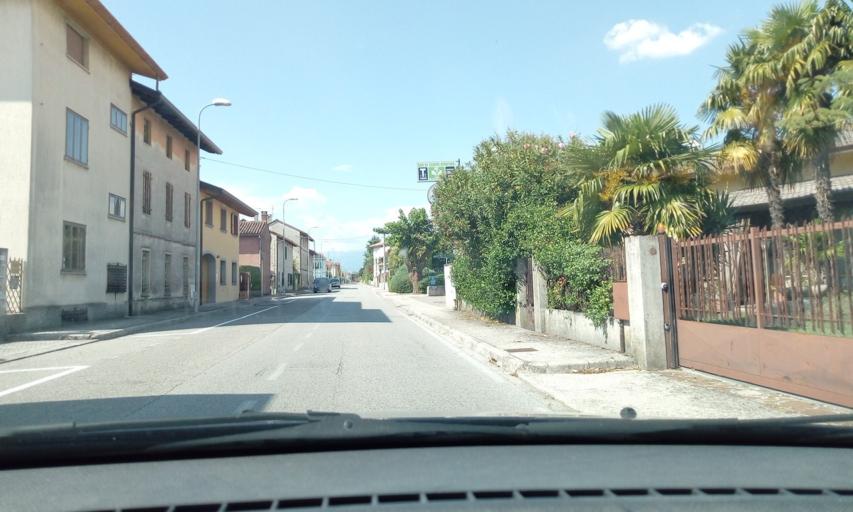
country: IT
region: Friuli Venezia Giulia
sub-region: Provincia di Udine
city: Pradamano
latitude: 46.0344
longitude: 13.3063
